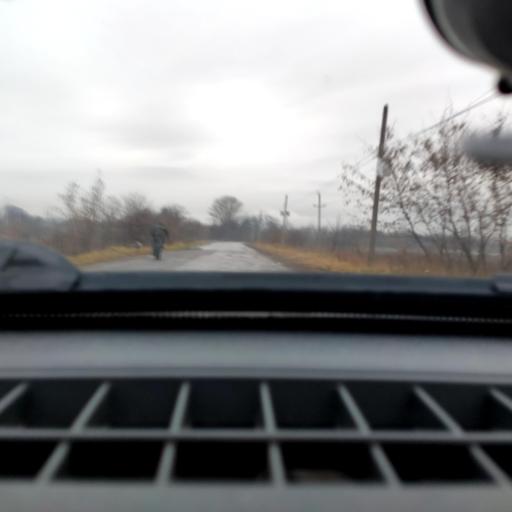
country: RU
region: Bashkortostan
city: Iglino
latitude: 54.8010
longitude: 56.1993
